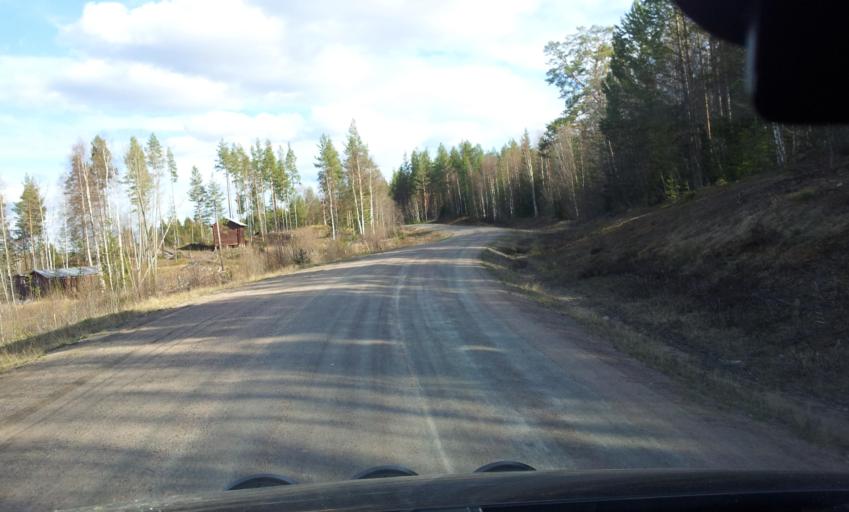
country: SE
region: Vaesternorrland
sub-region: Ange Kommun
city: Ange
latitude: 62.1766
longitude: 15.6347
